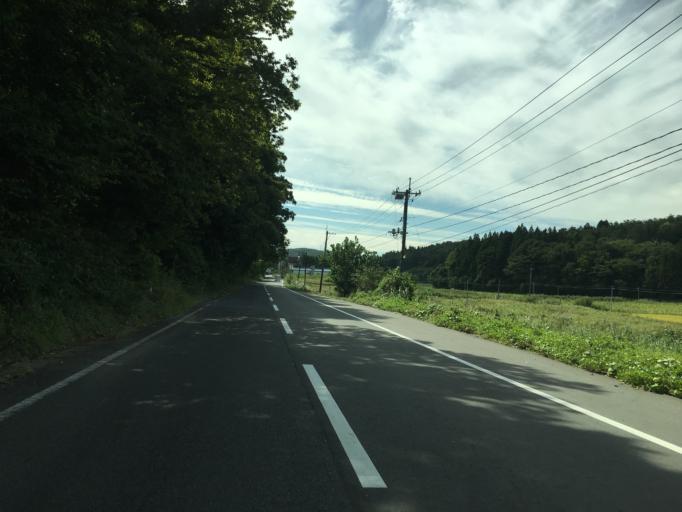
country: JP
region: Fukushima
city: Ishikawa
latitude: 37.2519
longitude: 140.5657
